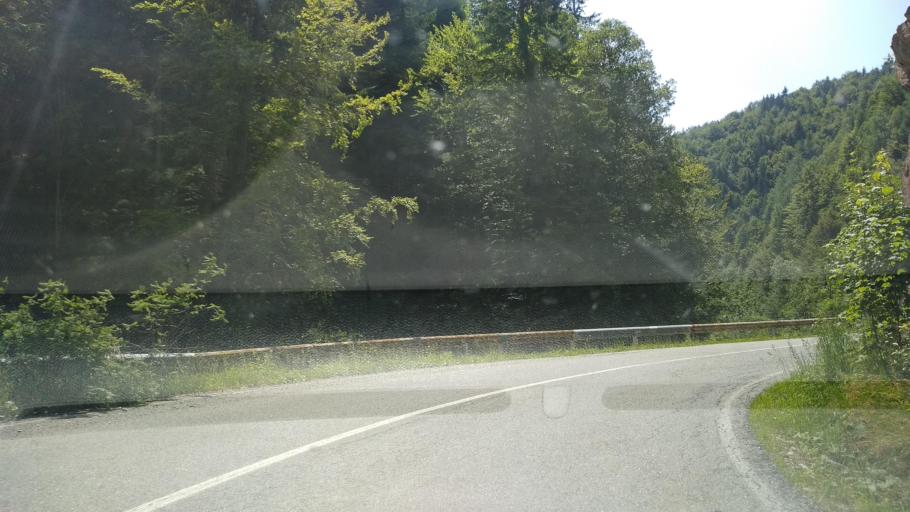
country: RO
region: Hunedoara
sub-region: Comuna Uricani
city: Uricani
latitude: 45.2811
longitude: 22.9667
